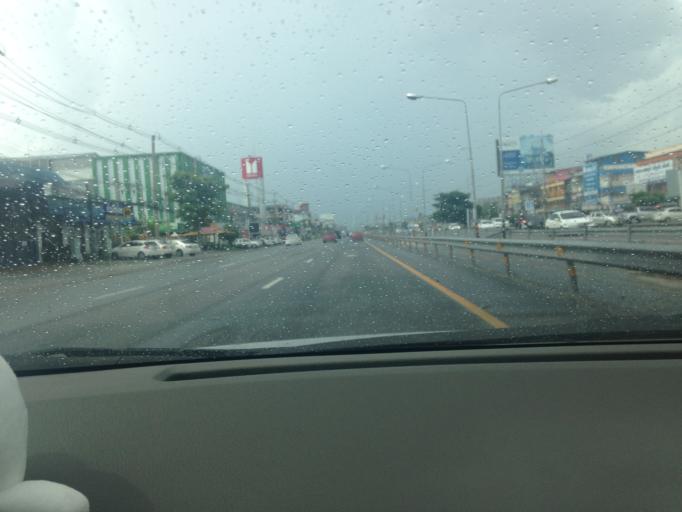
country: TH
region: Chon Buri
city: Chon Buri
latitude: 13.2982
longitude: 100.9467
